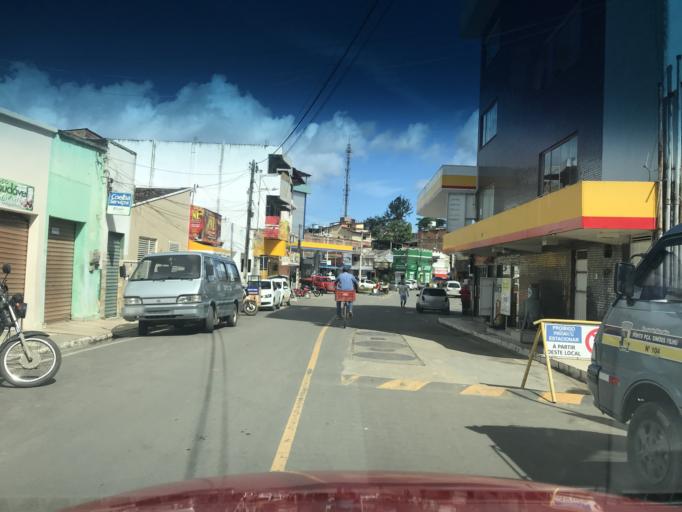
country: BR
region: Bahia
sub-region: Gandu
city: Gandu
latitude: -13.7443
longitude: -39.4859
